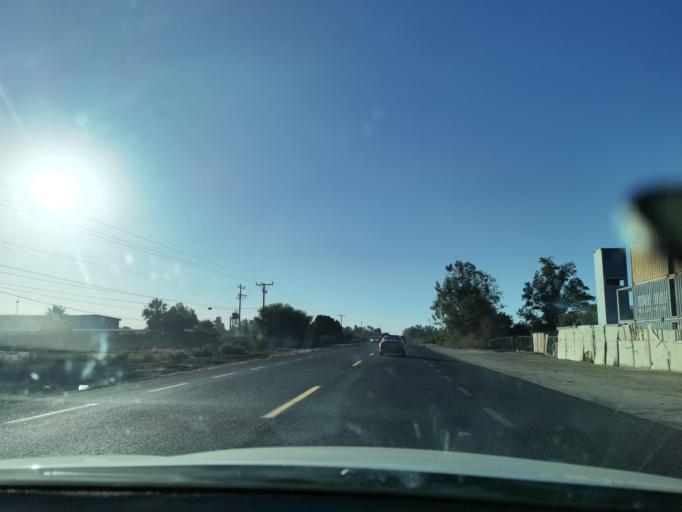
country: MX
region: Baja California
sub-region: Mexicali
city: Islas Agrarias Grupo A
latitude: 32.6441
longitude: -115.3148
